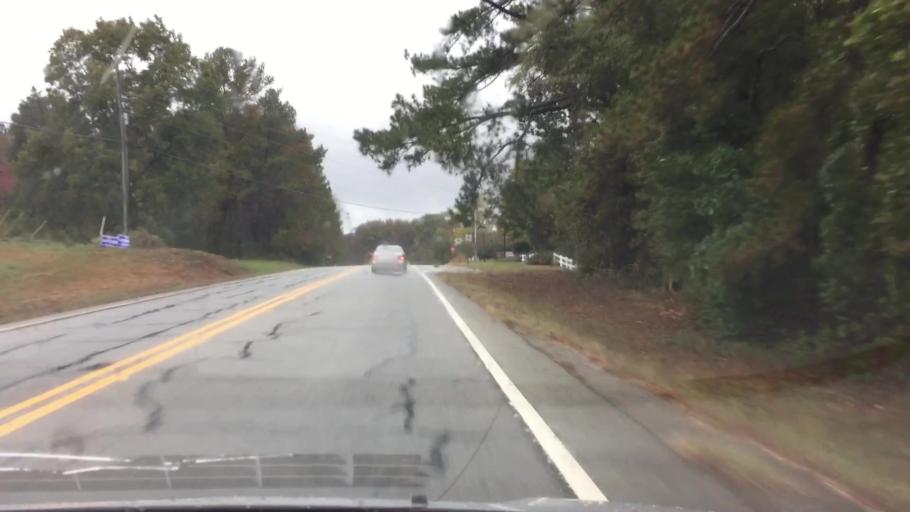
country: US
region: Georgia
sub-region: Henry County
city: Stockbridge
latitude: 33.5733
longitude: -84.1473
